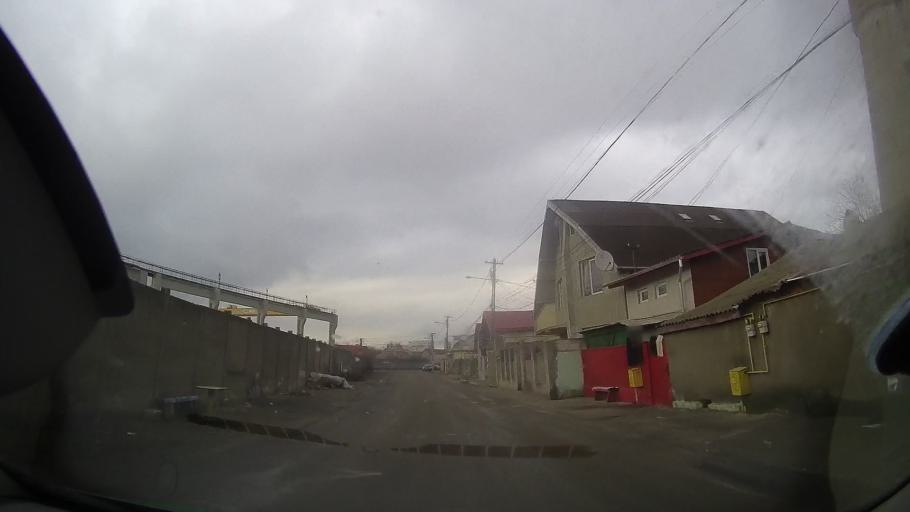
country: RO
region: Cluj
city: Turda
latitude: 46.5558
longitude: 23.7889
